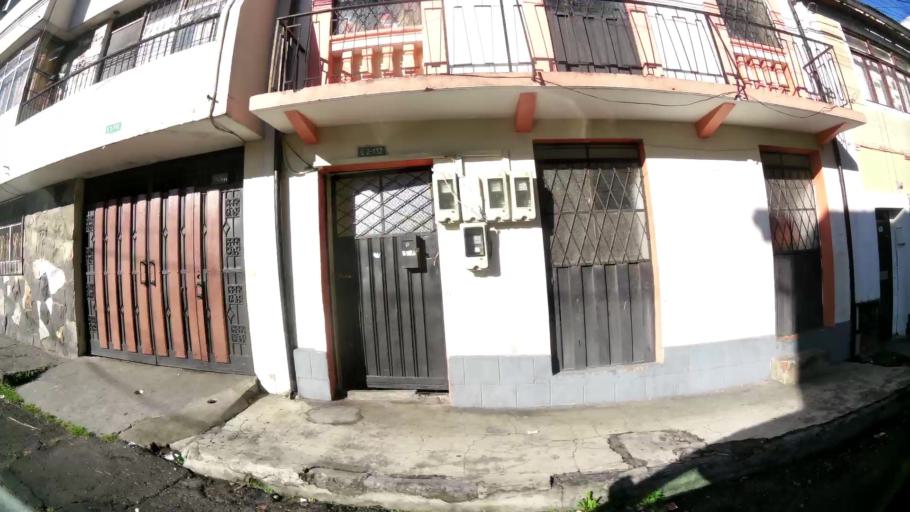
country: EC
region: Pichincha
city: Quito
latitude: -0.2412
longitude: -78.5158
